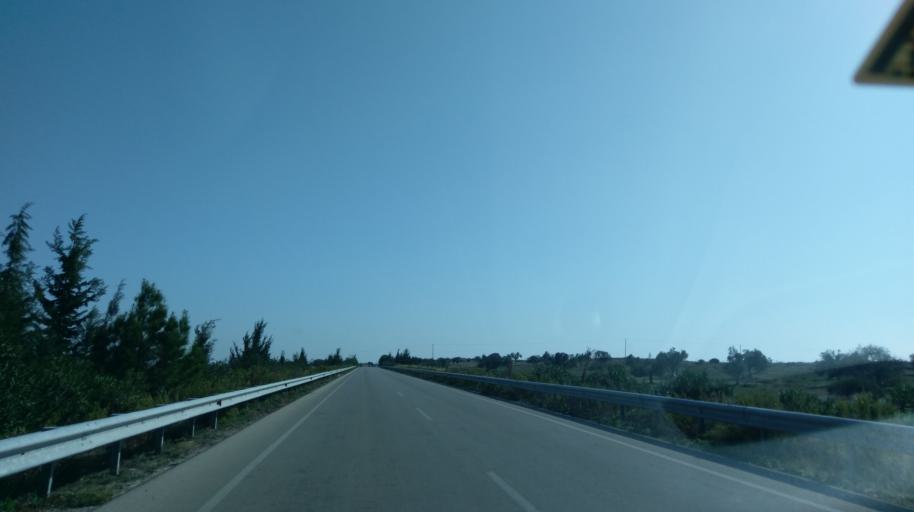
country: CY
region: Ammochostos
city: Leonarisso
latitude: 35.3950
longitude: 34.0044
